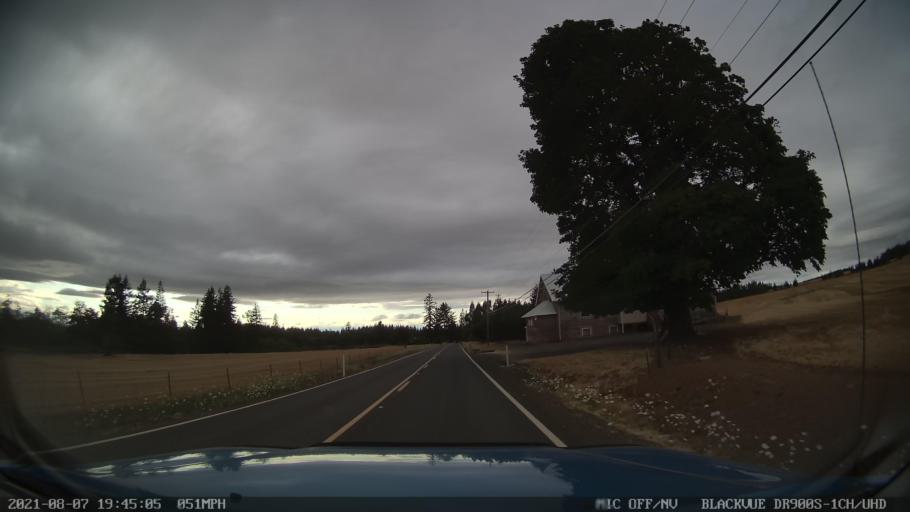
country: US
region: Oregon
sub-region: Marion County
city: Silverton
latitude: 44.9449
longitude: -122.6916
